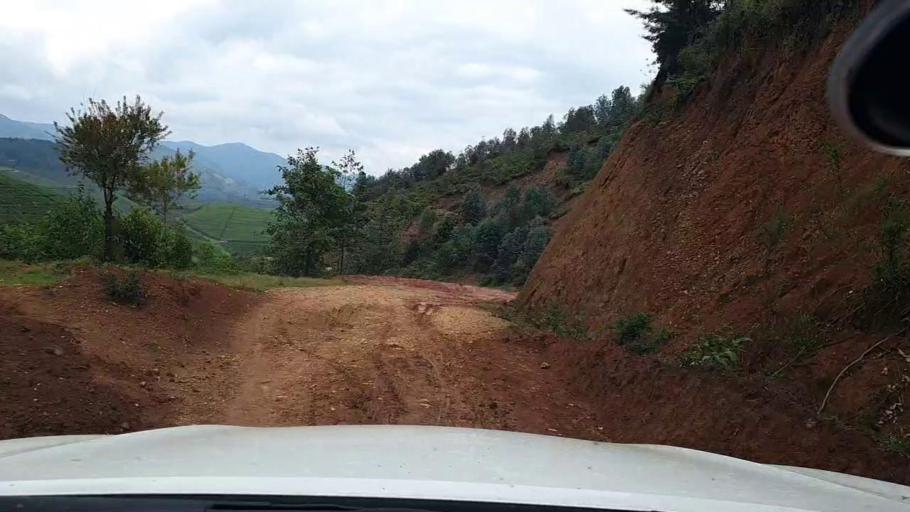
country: RW
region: Western Province
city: Kibuye
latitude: -2.1587
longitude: 29.4553
